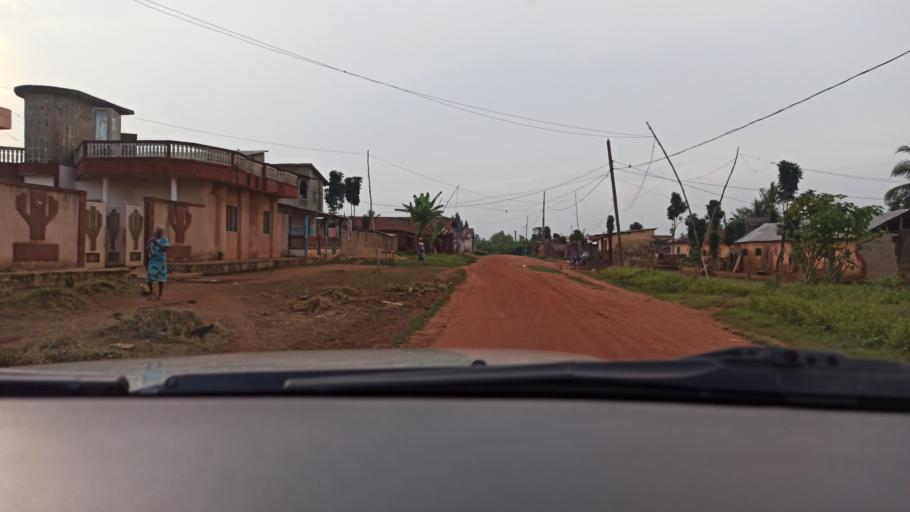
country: BJ
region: Queme
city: Porto-Novo
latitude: 6.5023
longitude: 2.6994
